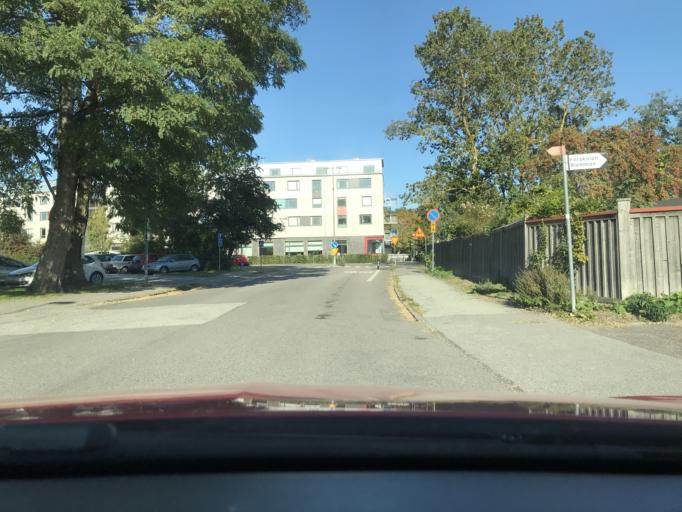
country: SE
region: Skane
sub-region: Lunds Kommun
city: Lund
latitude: 55.6939
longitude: 13.2053
